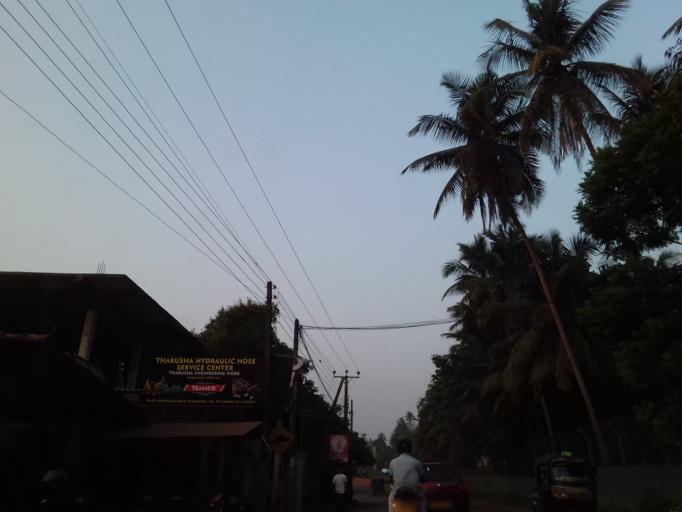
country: LK
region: Western
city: Welisara
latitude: 7.0299
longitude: 79.9602
